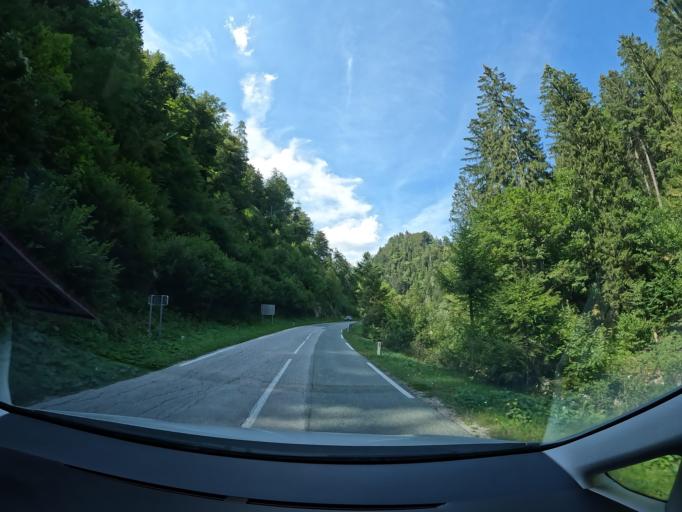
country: SI
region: Kranj
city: Golnik
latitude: 46.3856
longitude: 14.3711
